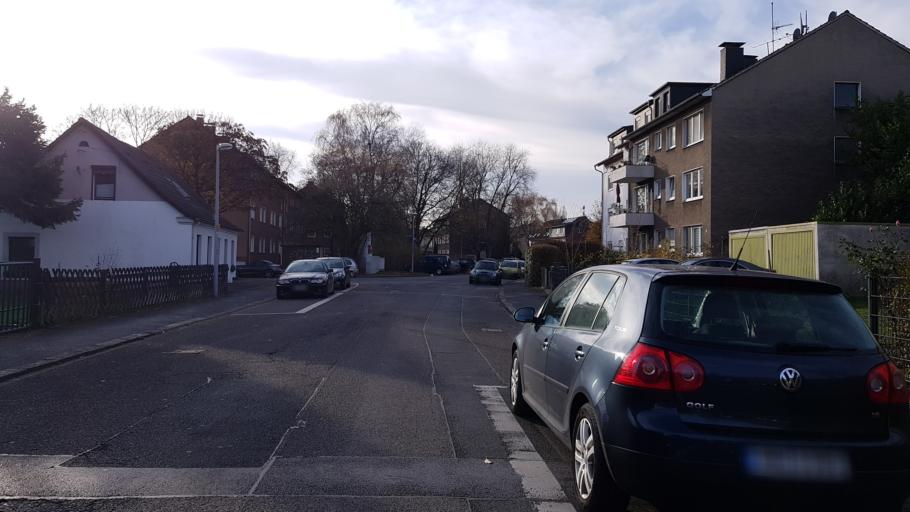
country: DE
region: North Rhine-Westphalia
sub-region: Regierungsbezirk Dusseldorf
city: Oberhausen
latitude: 51.4539
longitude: 6.8664
